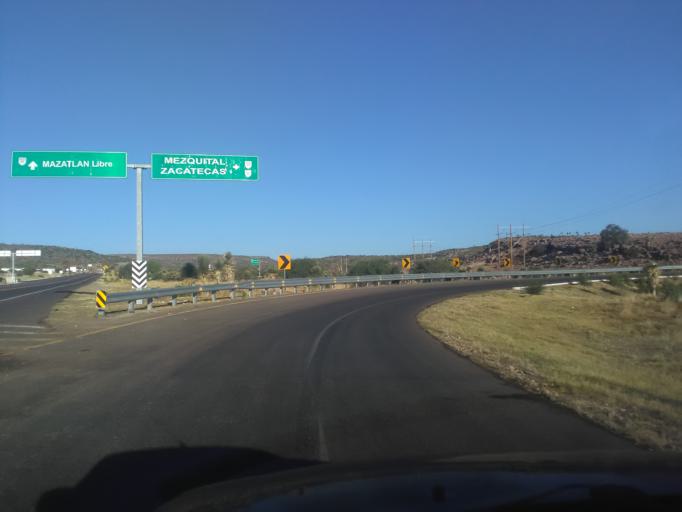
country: MX
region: Durango
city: Victoria de Durango
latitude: 23.9968
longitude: -104.7259
